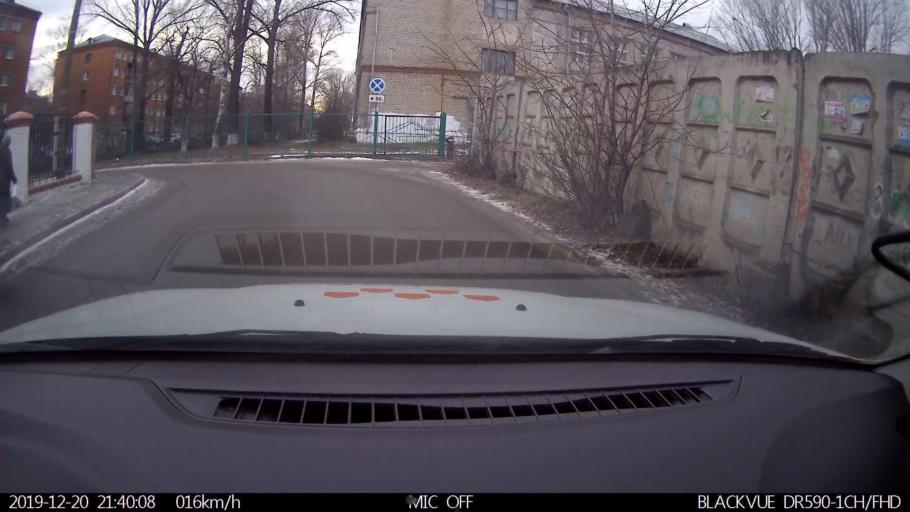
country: RU
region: Nizjnij Novgorod
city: Nizhniy Novgorod
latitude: 56.3324
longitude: 43.9567
